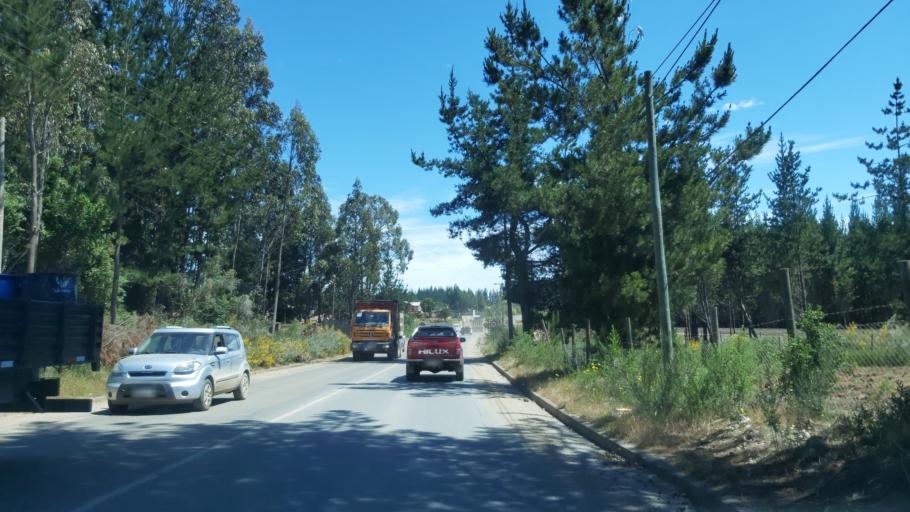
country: CL
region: Maule
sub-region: Provincia de Talca
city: Constitucion
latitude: -35.3906
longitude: -72.4243
